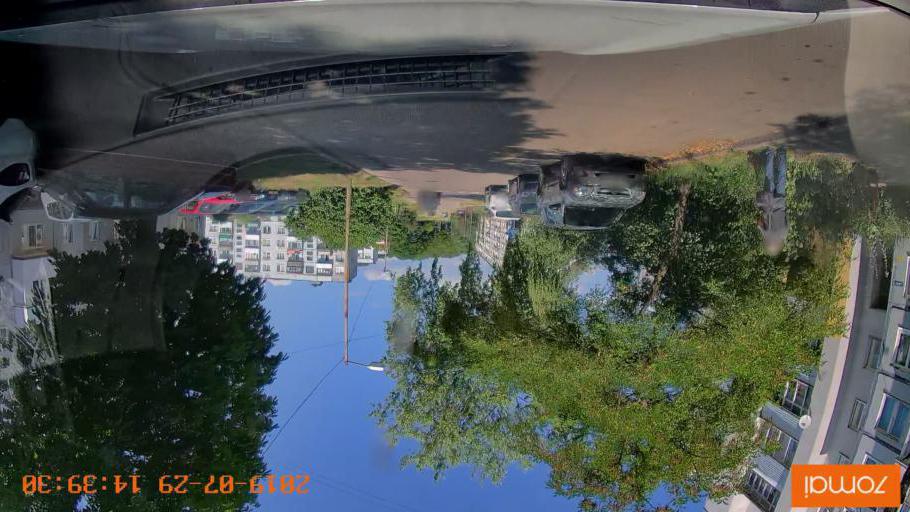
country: RU
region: Kaliningrad
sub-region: Gorod Kaliningrad
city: Baltiysk
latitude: 54.6520
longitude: 19.9030
